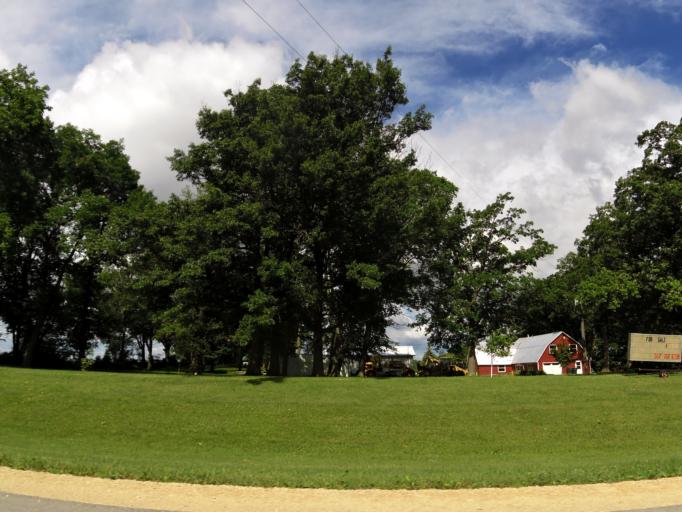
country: US
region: Minnesota
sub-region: Olmsted County
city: Stewartville
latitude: 43.8418
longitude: -92.4896
